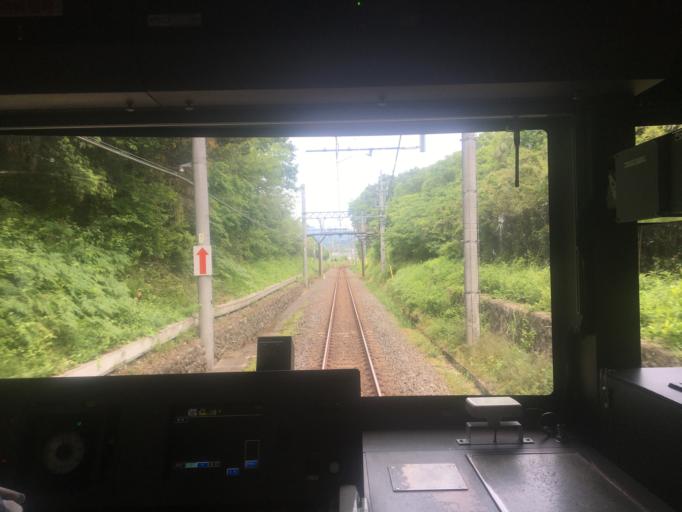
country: JP
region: Saitama
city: Ogawa
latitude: 36.0522
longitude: 139.2849
